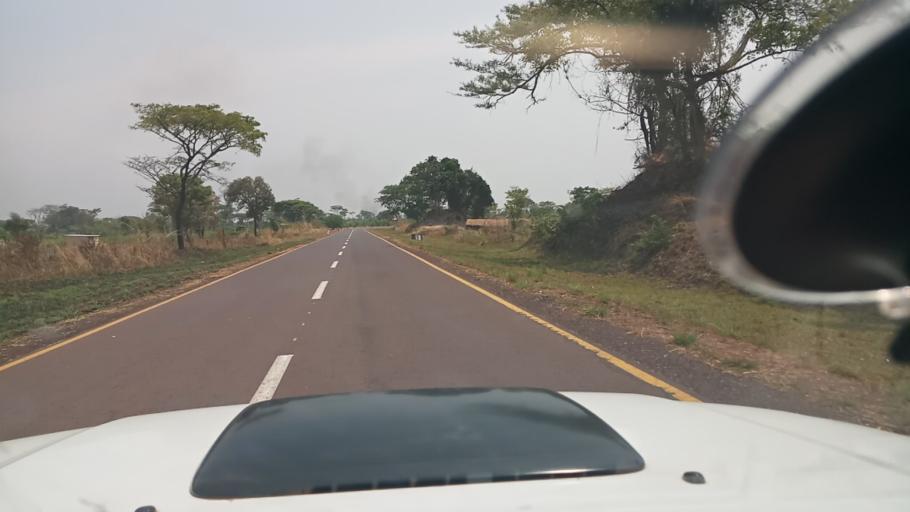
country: ZM
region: Luapula
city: Mwense
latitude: -10.7969
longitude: 28.2319
